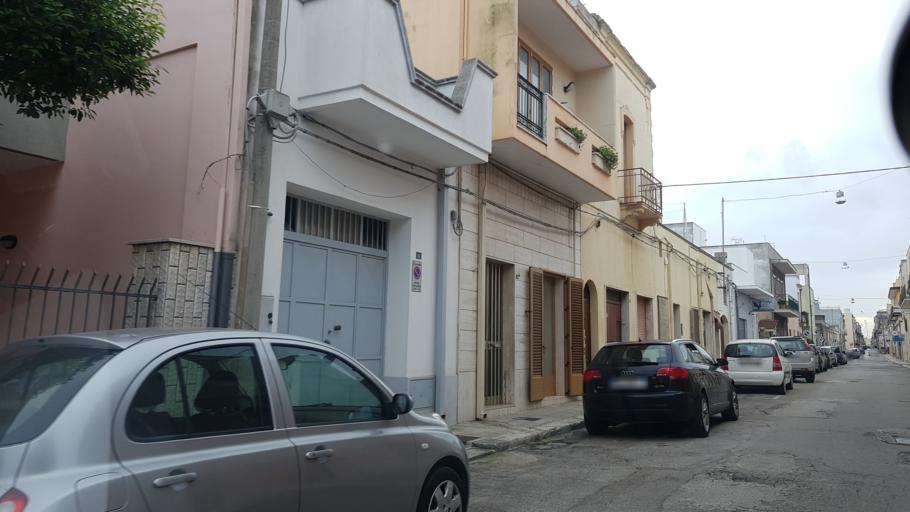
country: IT
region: Apulia
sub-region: Provincia di Brindisi
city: Mesagne
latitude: 40.5635
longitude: 17.8107
